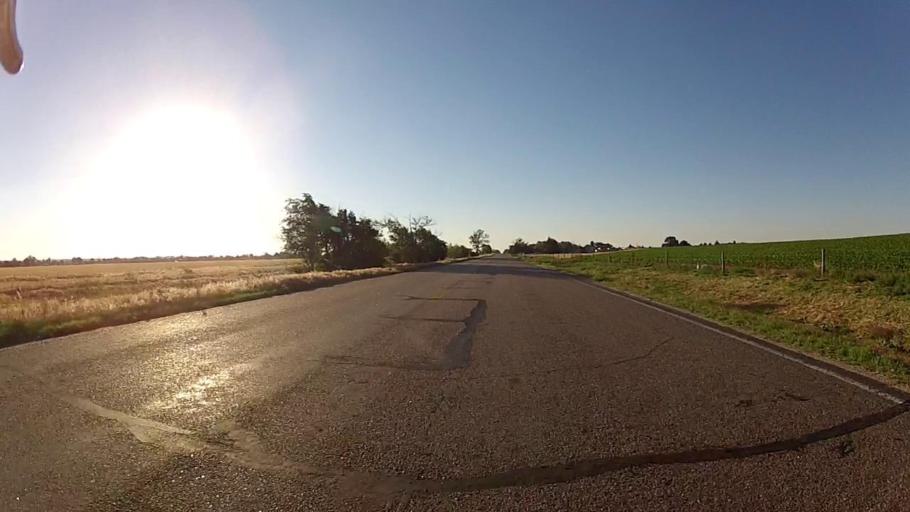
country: US
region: Kansas
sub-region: Ford County
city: Dodge City
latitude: 37.7178
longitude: -99.9414
